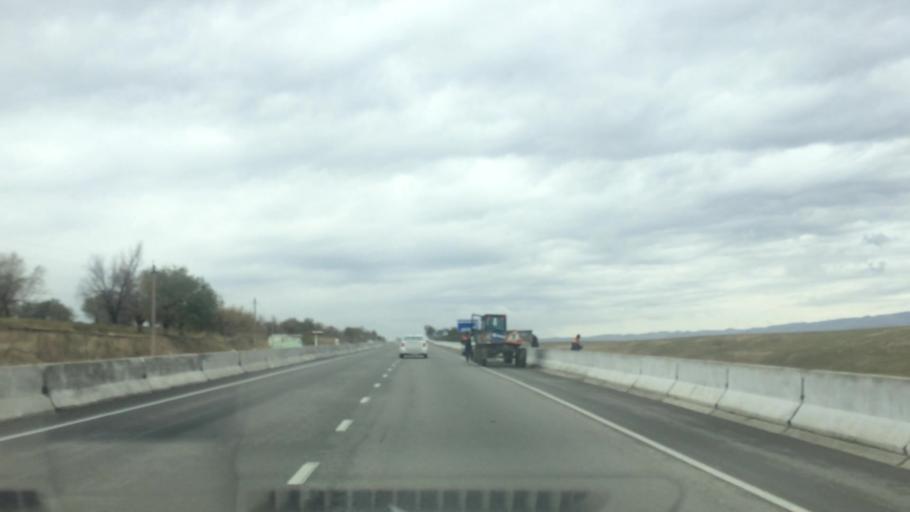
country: UZ
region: Samarqand
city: Bulung'ur
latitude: 39.9463
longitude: 67.5333
